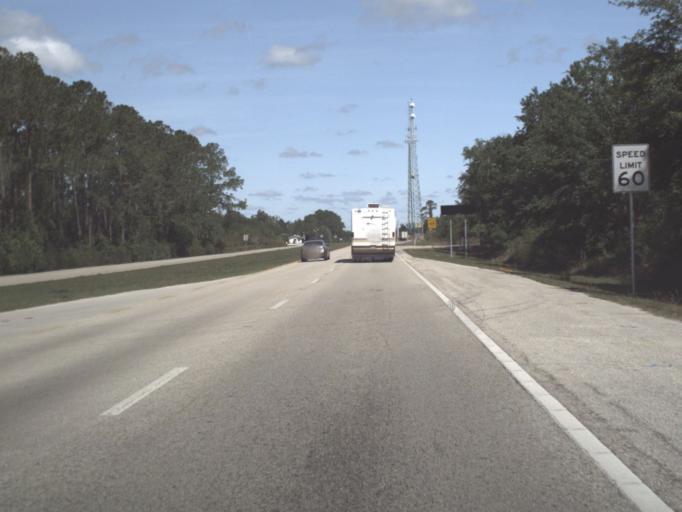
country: US
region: Florida
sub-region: Flagler County
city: Palm Coast
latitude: 29.5562
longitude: -81.2666
